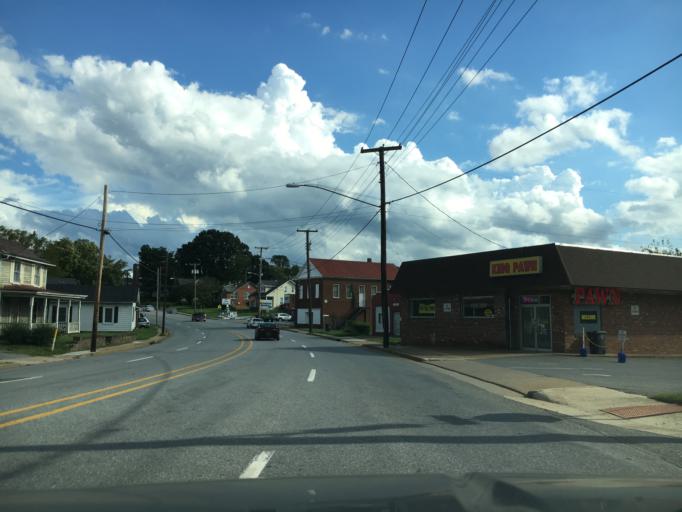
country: US
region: Virginia
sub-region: City of Lynchburg
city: Lynchburg
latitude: 37.3908
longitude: -79.1476
